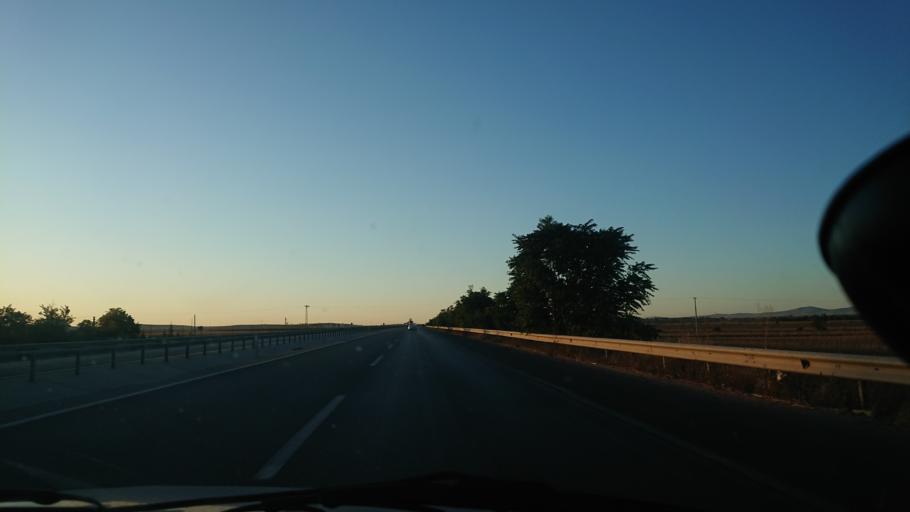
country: TR
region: Eskisehir
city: Mahmudiye
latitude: 39.5417
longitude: 30.9380
